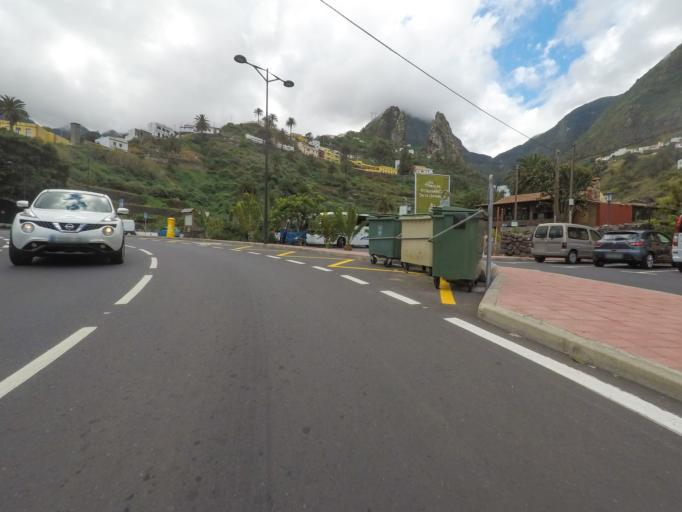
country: ES
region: Canary Islands
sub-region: Provincia de Santa Cruz de Tenerife
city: Hermigua
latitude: 28.1536
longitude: -17.1991
